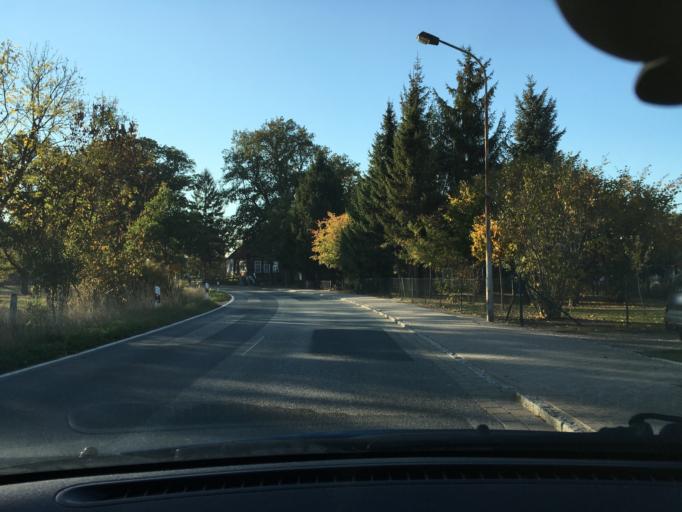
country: DE
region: Lower Saxony
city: Neu Darchau
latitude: 53.2879
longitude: 10.8788
